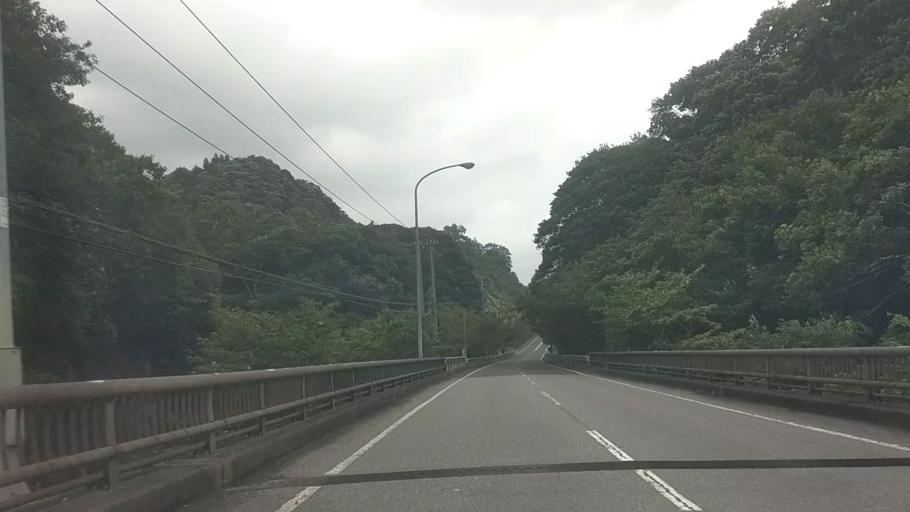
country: JP
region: Chiba
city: Kimitsu
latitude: 35.2326
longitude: 139.9673
